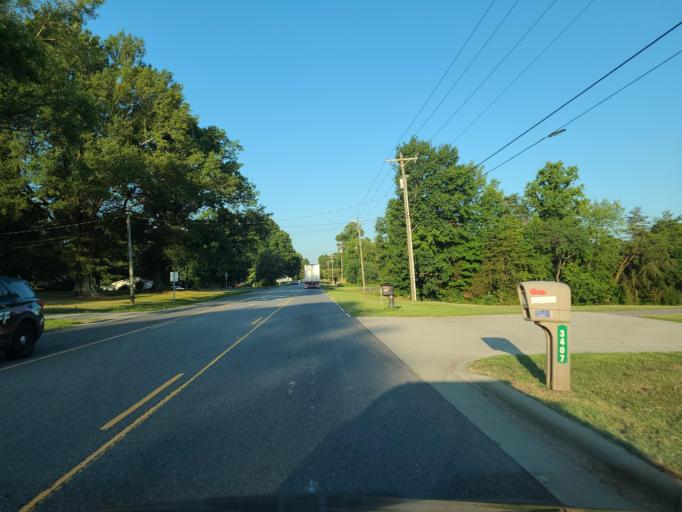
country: US
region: North Carolina
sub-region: Catawba County
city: Mountain View
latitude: 35.6789
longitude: -81.3810
